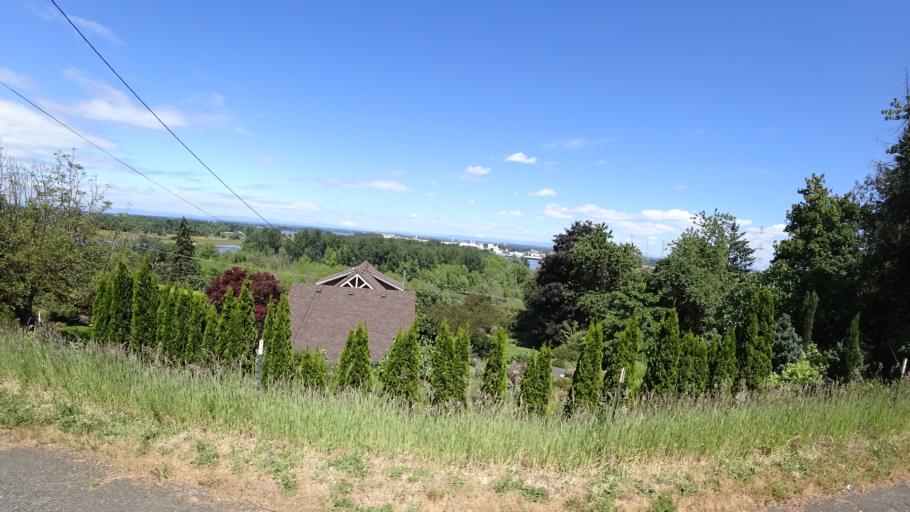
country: US
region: Oregon
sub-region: Washington County
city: Oak Hills
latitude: 45.6149
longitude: -122.8037
